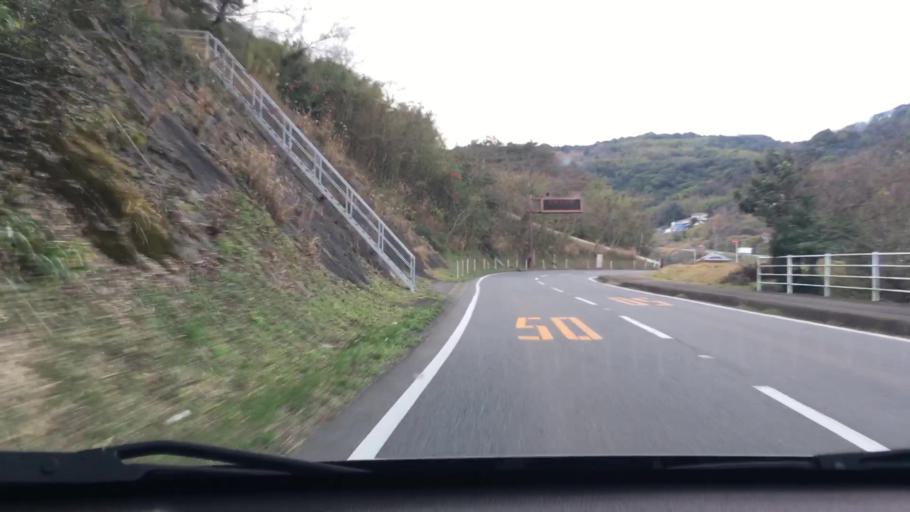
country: JP
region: Oita
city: Hiji
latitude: 33.3609
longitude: 131.4908
